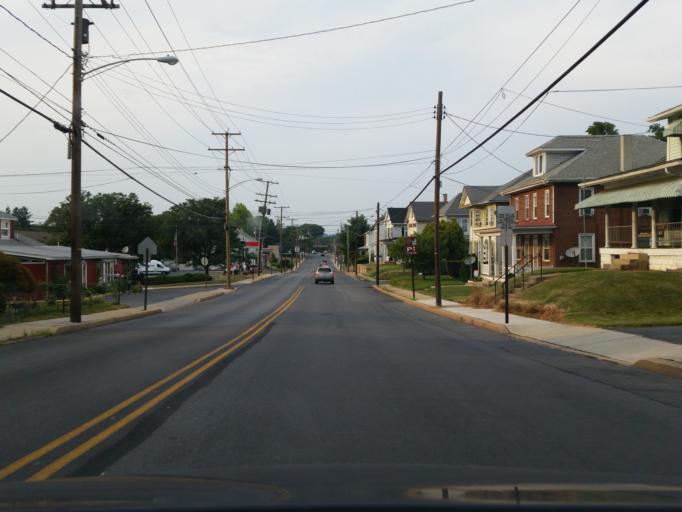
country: US
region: Pennsylvania
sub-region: Lebanon County
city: Pleasant Hill
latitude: 40.3264
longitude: -76.4264
